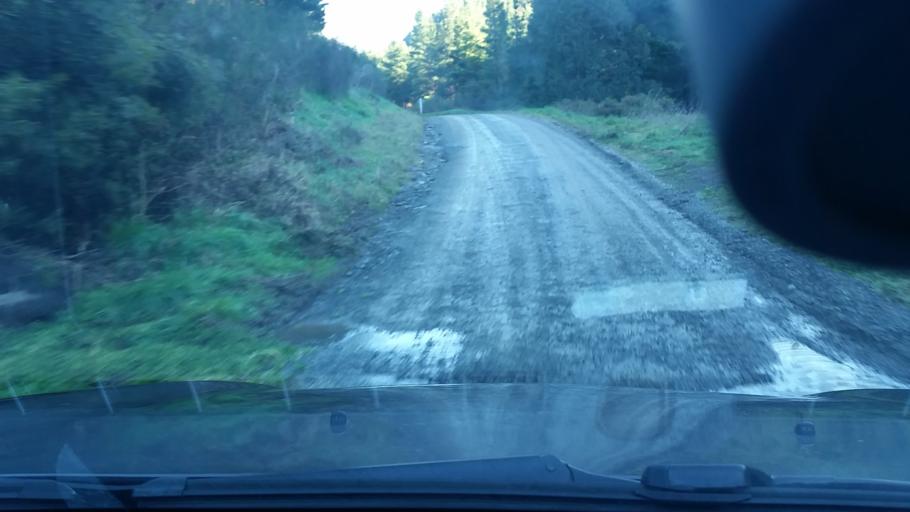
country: NZ
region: Marlborough
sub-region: Marlborough District
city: Blenheim
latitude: -41.6119
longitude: 173.9694
